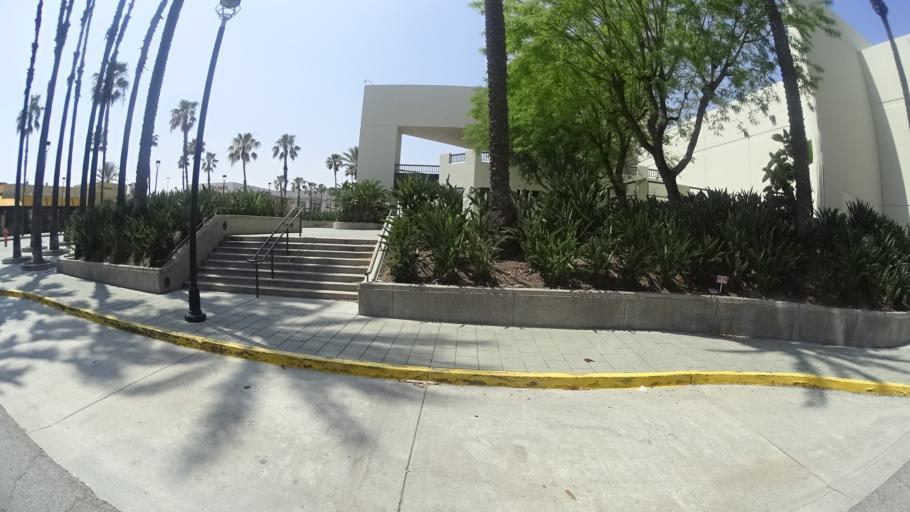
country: US
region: California
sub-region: Los Angeles County
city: Burbank
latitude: 34.1847
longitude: -118.3134
